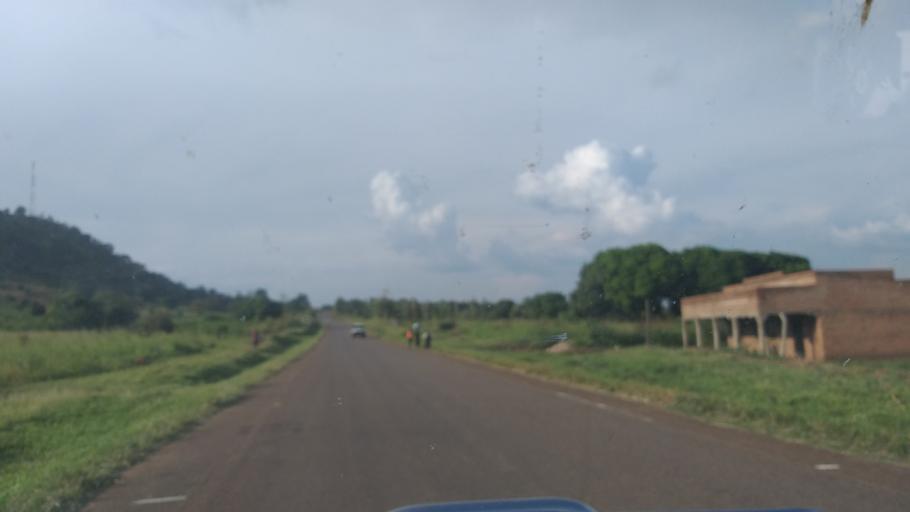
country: UG
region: Northern Region
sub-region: Arua District
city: Arua
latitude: 2.8320
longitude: 30.9943
